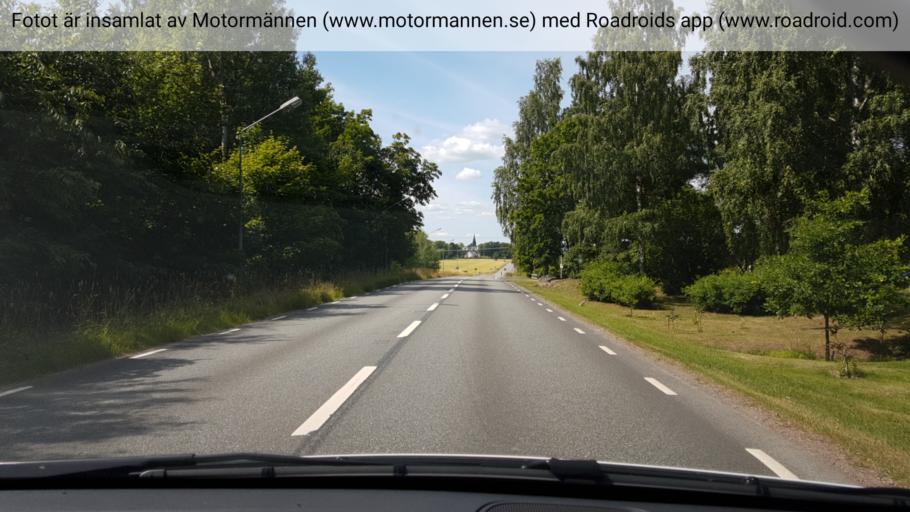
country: SE
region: Vaestra Goetaland
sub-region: Toreboda Kommun
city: Toereboda
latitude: 58.6074
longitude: 14.0309
